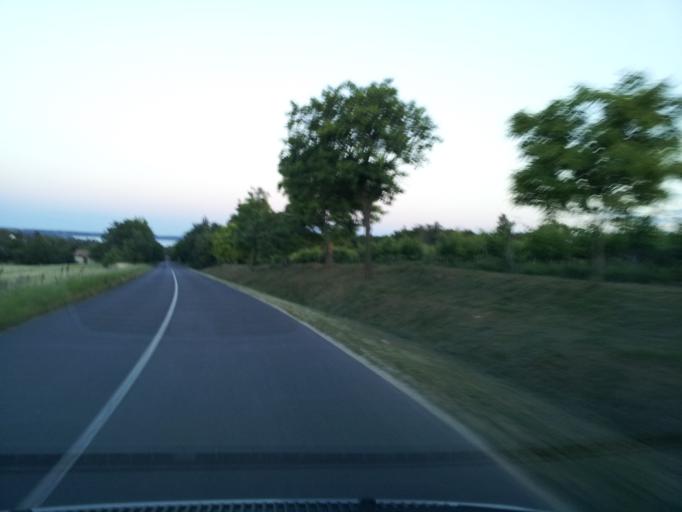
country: HU
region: Veszprem
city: Balatonkenese
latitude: 47.0485
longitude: 18.0914
